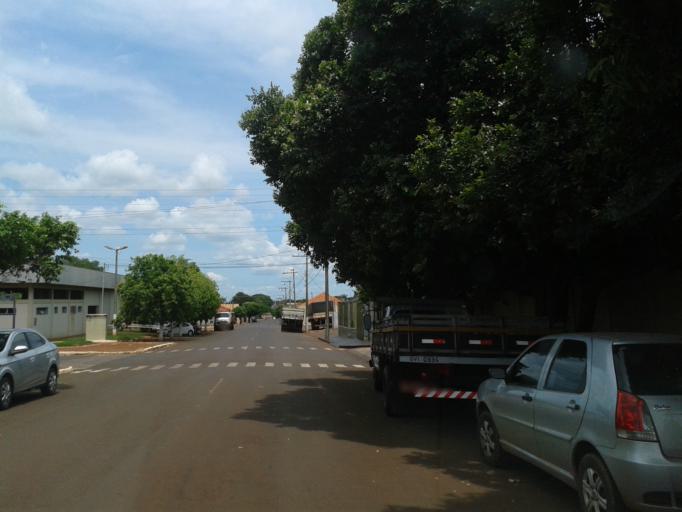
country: BR
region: Minas Gerais
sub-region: Centralina
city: Centralina
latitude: -18.7228
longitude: -49.2007
